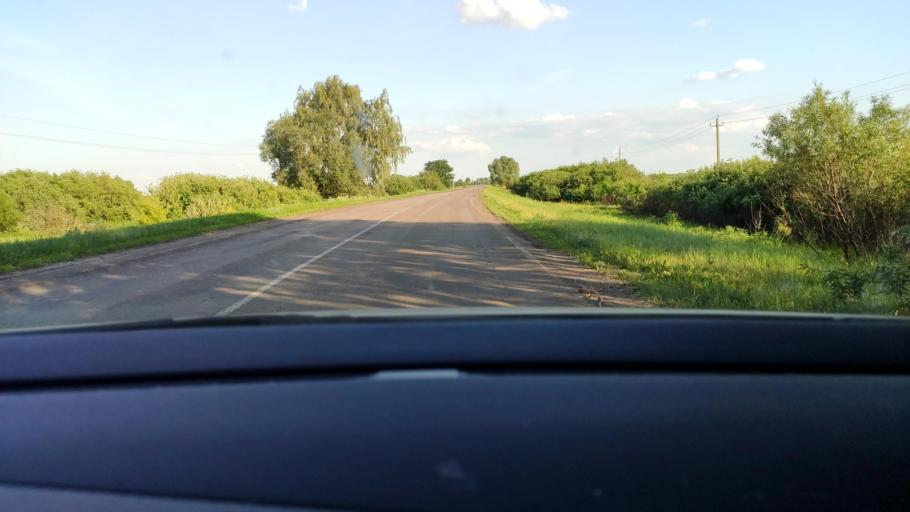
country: RU
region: Voronezj
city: Kashirskoye
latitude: 51.4894
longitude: 39.8509
